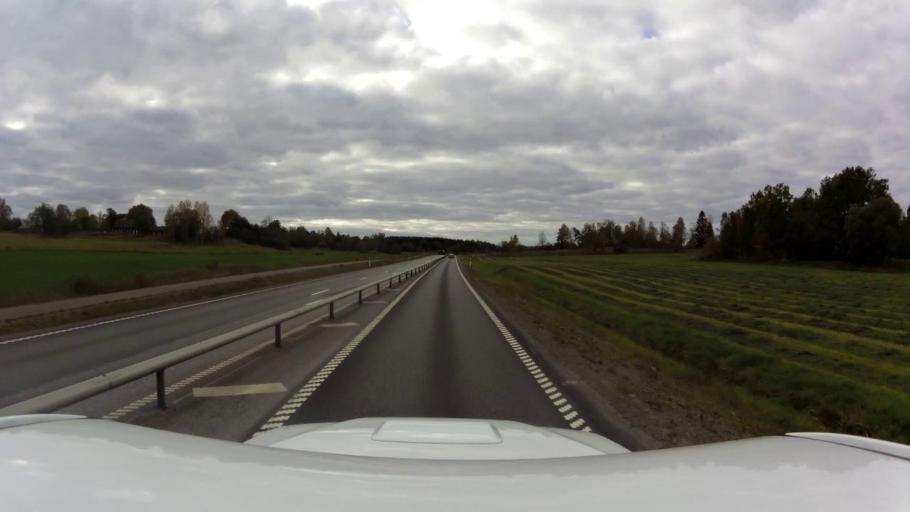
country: SE
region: OEstergoetland
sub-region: Linkopings Kommun
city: Malmslatt
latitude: 58.3133
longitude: 15.5672
